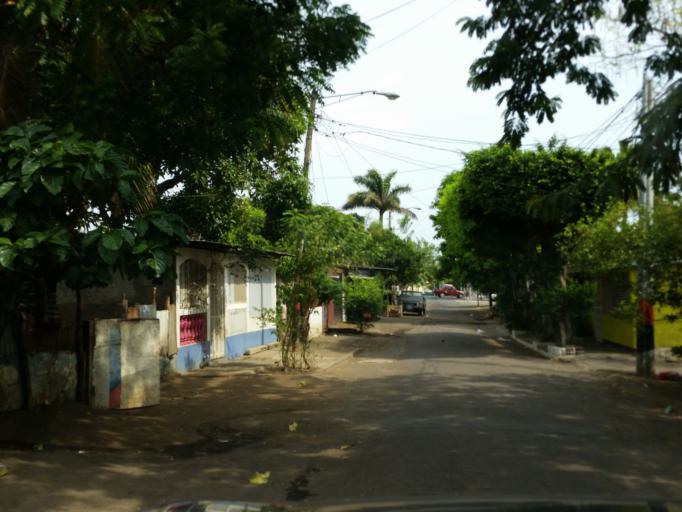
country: NI
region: Managua
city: Managua
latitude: 12.1135
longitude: -86.2538
